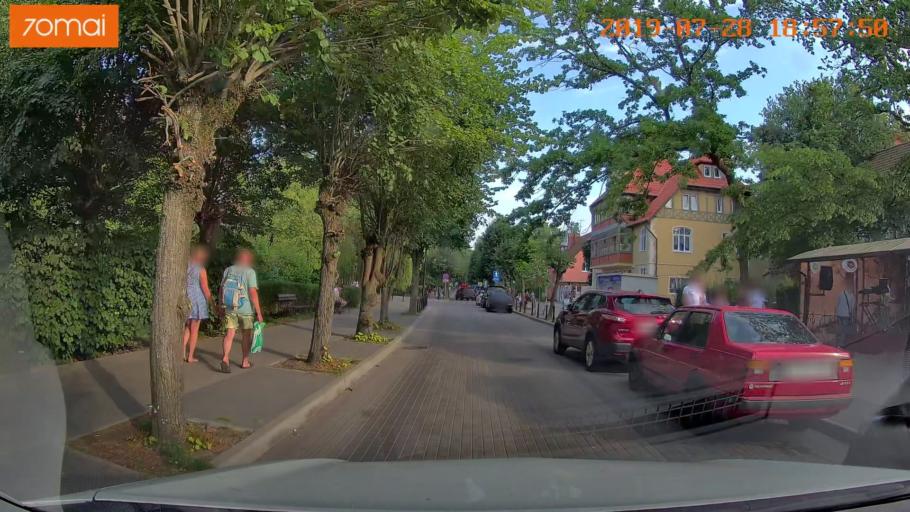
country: RU
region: Kaliningrad
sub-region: Gorod Svetlogorsk
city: Svetlogorsk
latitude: 54.9433
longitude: 20.1541
